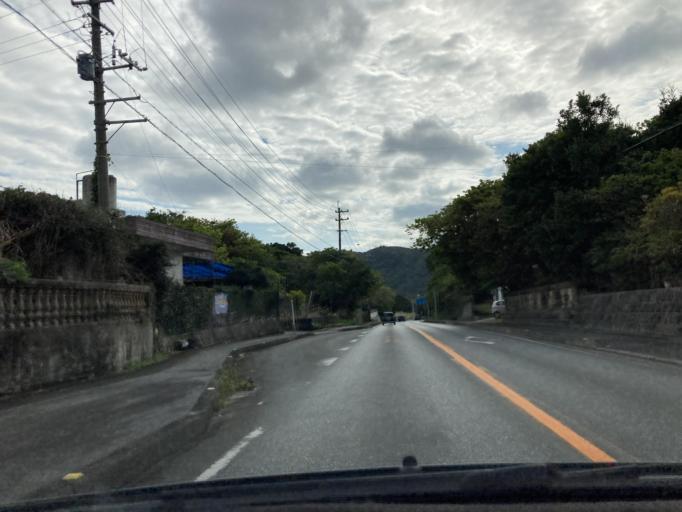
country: JP
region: Okinawa
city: Nago
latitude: 26.6569
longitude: 127.9843
